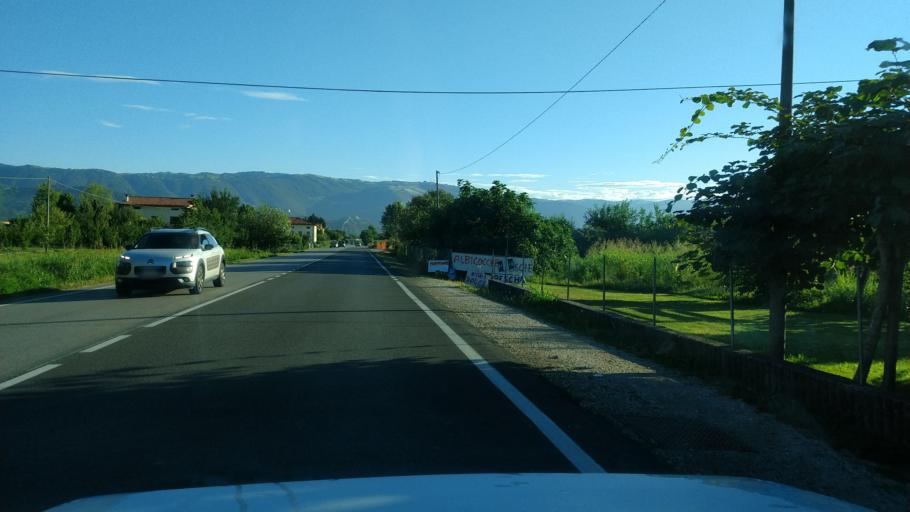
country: IT
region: Veneto
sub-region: Provincia di Vicenza
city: Schiavon
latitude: 45.7127
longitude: 11.6496
